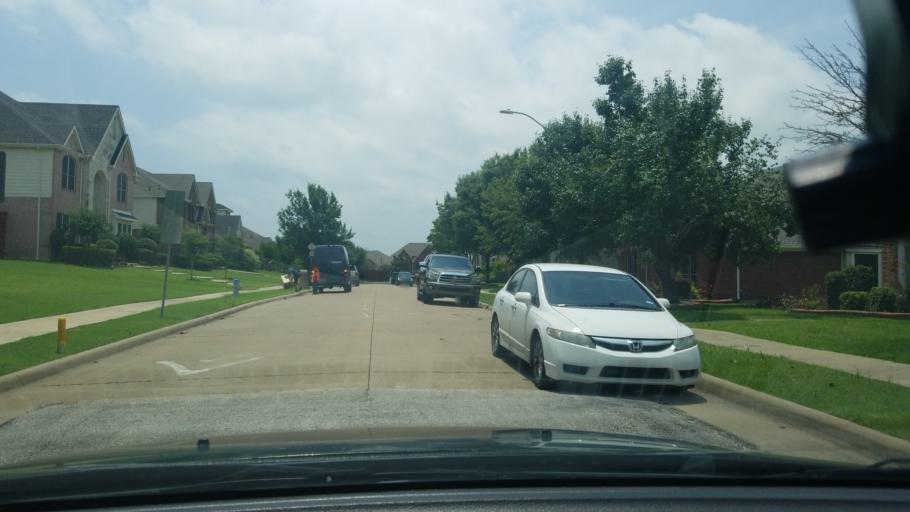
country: US
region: Texas
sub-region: Dallas County
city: Sunnyvale
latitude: 32.8112
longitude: -96.6001
